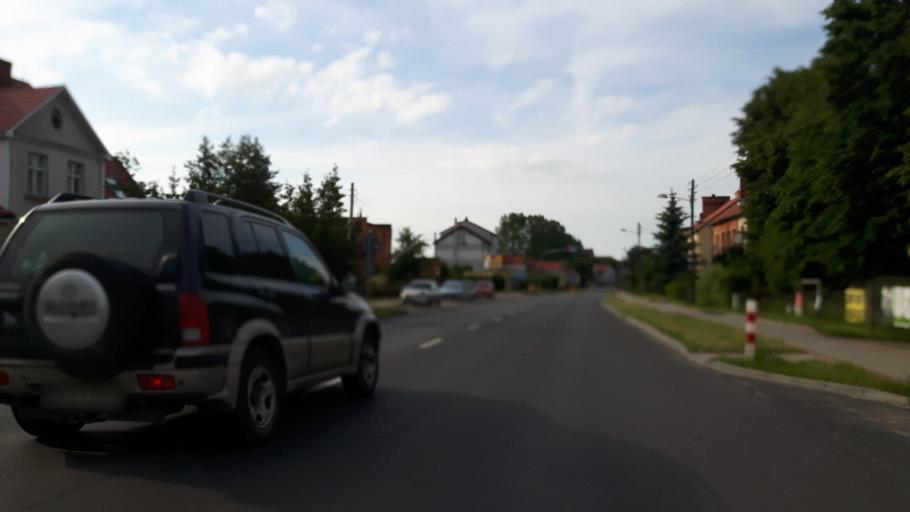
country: PL
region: West Pomeranian Voivodeship
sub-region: Powiat gryficki
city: Gryfice
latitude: 53.9062
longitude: 15.2013
